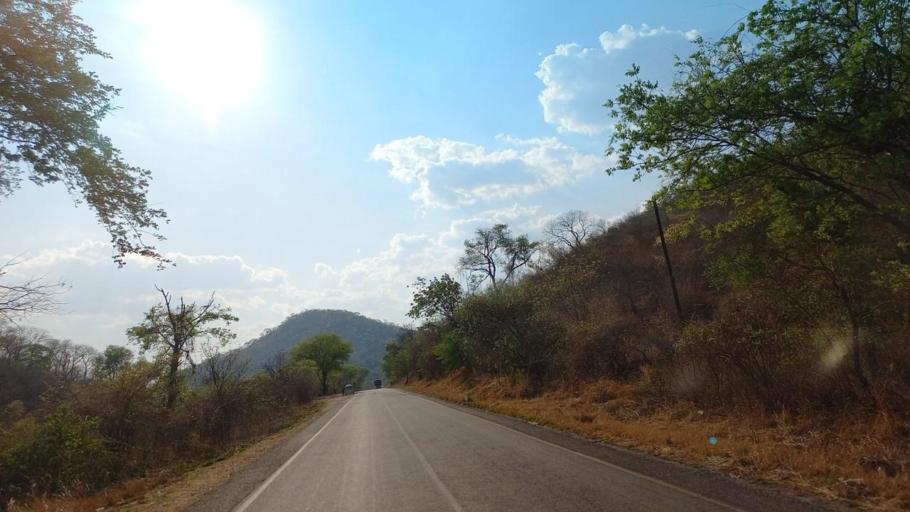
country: ZM
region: Lusaka
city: Luangwa
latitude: -14.9856
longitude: 30.1929
